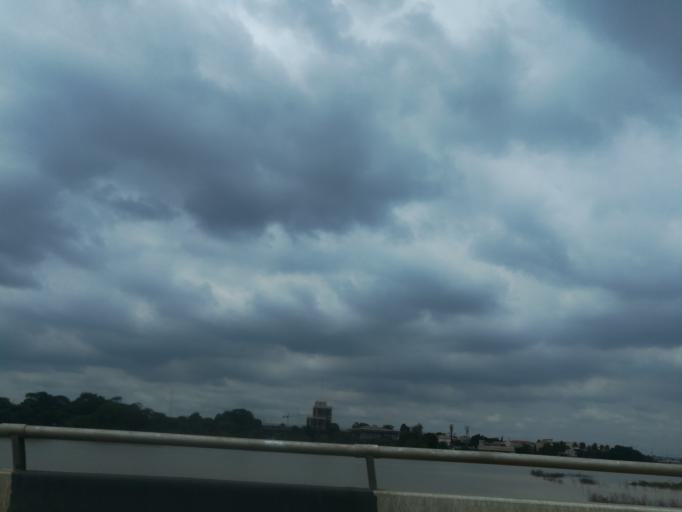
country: NG
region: Lagos
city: Makoko
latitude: 6.5206
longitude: 3.4050
